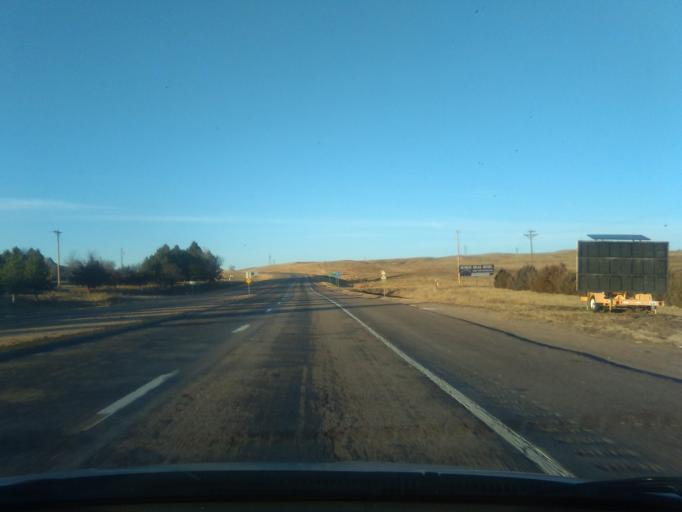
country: US
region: Nebraska
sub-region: Cheyenne County
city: Sidney
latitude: 41.1498
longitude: -102.9452
